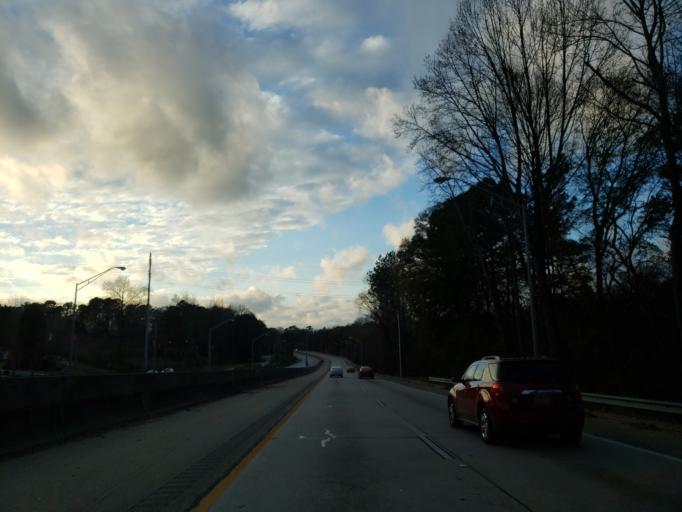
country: US
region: Georgia
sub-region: Fulton County
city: East Point
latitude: 33.6986
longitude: -84.4503
